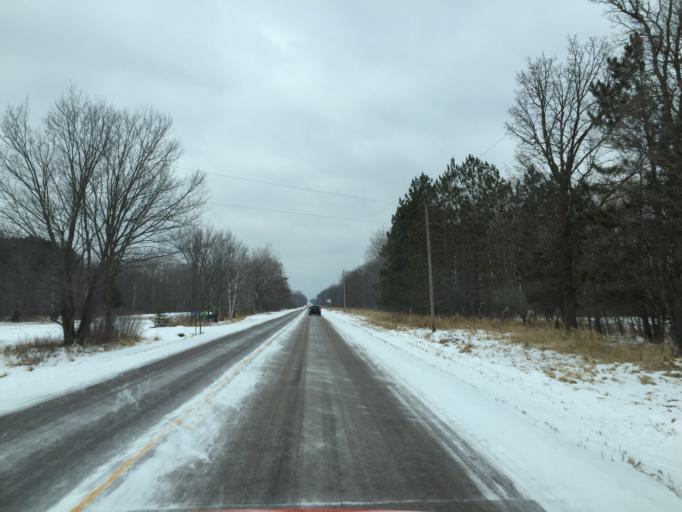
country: US
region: Minnesota
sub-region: Mille Lacs County
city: Vineland
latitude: 46.0776
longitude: -93.7624
